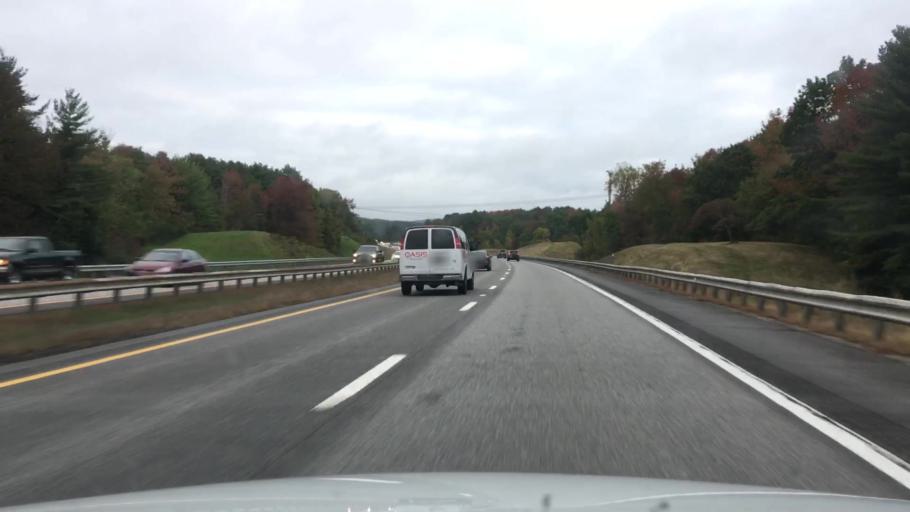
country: US
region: Maine
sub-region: Cumberland County
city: Cumberland Center
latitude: 43.7550
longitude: -70.3047
